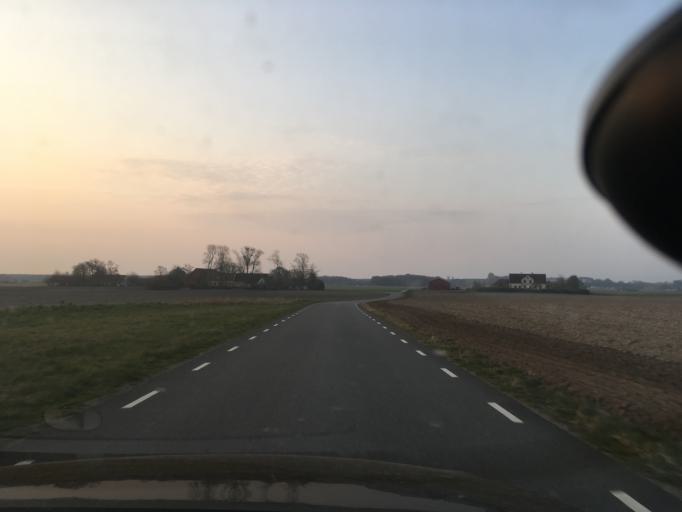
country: SE
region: Skane
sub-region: Ystads Kommun
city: Kopingebro
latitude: 55.4122
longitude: 14.1523
